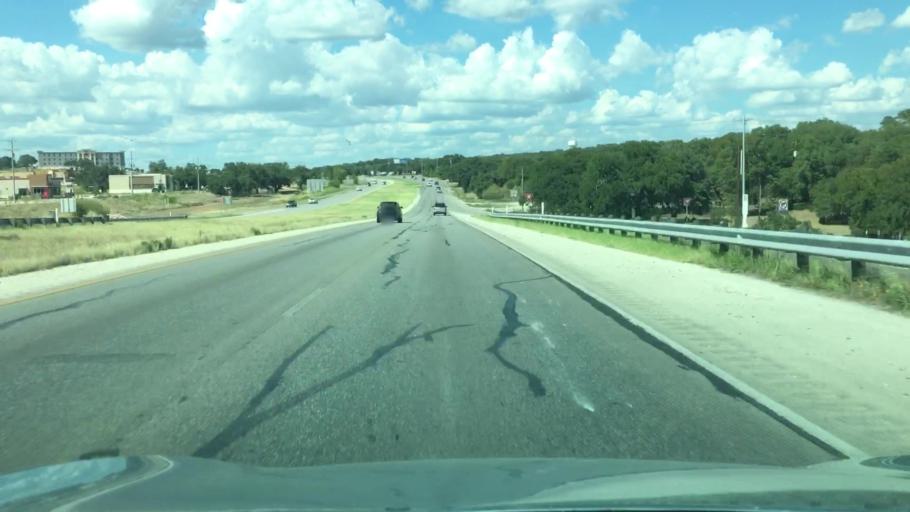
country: US
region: Texas
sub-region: Comal County
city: Bulverde
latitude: 29.7982
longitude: -98.4183
